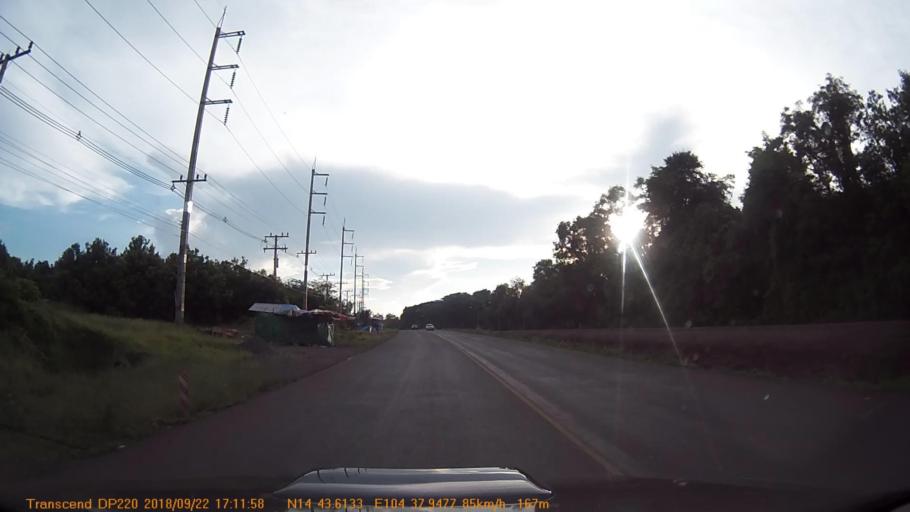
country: TH
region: Sisaket
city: Benchalak
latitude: 14.7268
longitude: 104.6322
